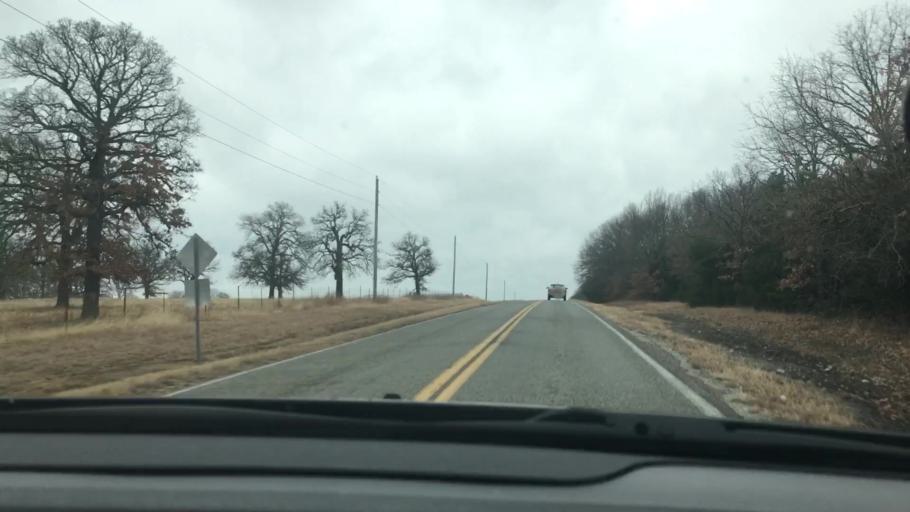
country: US
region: Oklahoma
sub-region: Johnston County
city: Tishomingo
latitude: 34.1959
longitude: -96.5777
